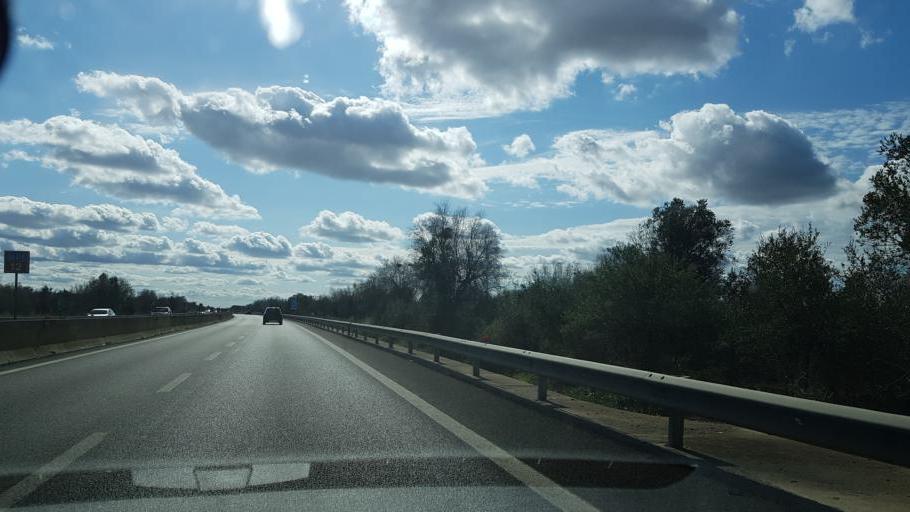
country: IT
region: Apulia
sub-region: Provincia di Lecce
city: Trepuzzi
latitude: 40.4250
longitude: 18.0908
